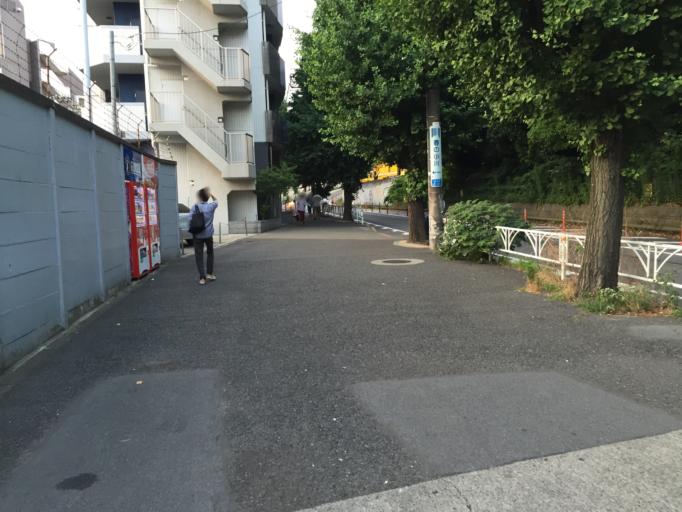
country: JP
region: Tokyo
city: Tokyo
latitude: 35.6769
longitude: 139.6928
